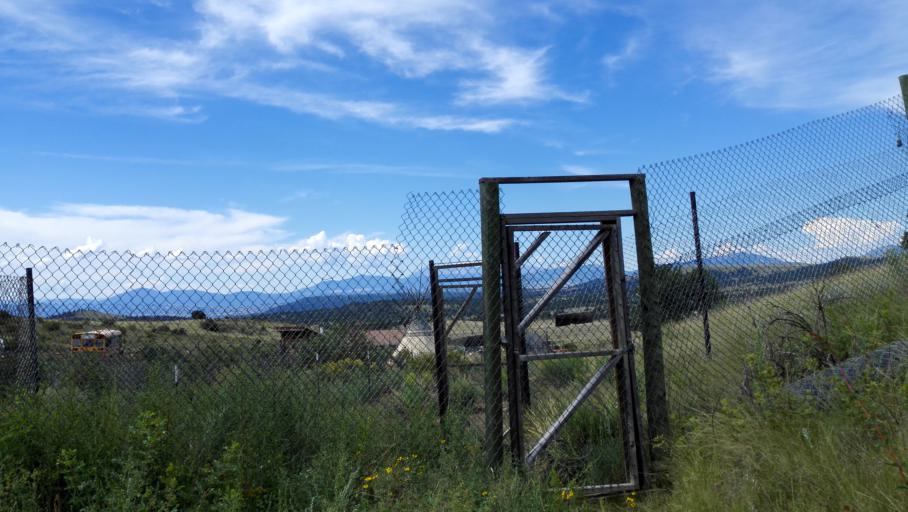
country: US
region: Colorado
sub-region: Custer County
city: Westcliffe
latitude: 37.9614
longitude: -105.2151
